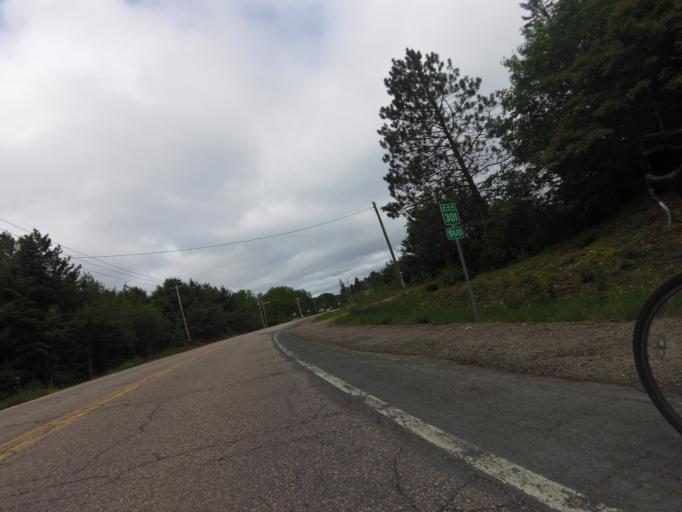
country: CA
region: Quebec
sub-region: Outaouais
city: Shawville
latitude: 45.8379
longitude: -76.4452
